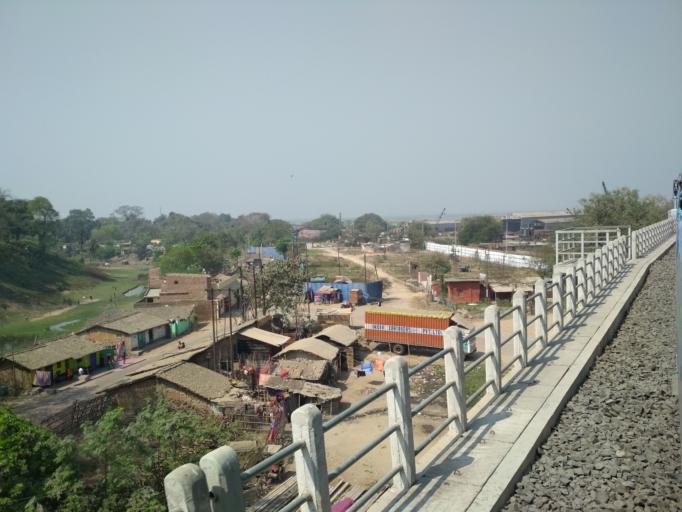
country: IN
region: Bihar
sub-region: Munger
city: Munger
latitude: 25.3870
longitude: 86.4693
